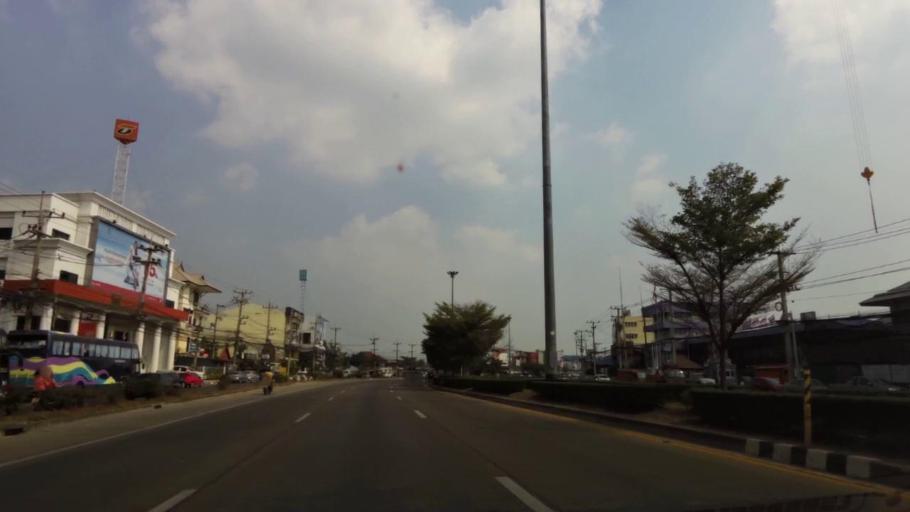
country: TH
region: Phra Nakhon Si Ayutthaya
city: Phra Nakhon Si Ayutthaya
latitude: 14.3548
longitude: 100.5974
